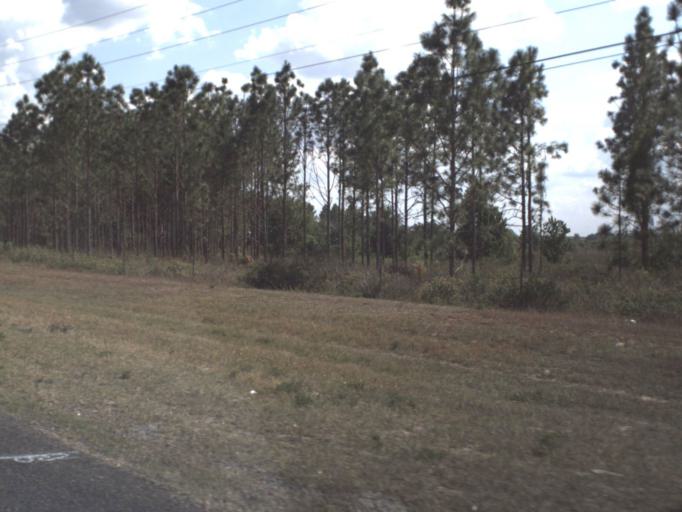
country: US
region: Florida
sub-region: Lake County
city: Yalaha
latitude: 28.6594
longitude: -81.8491
